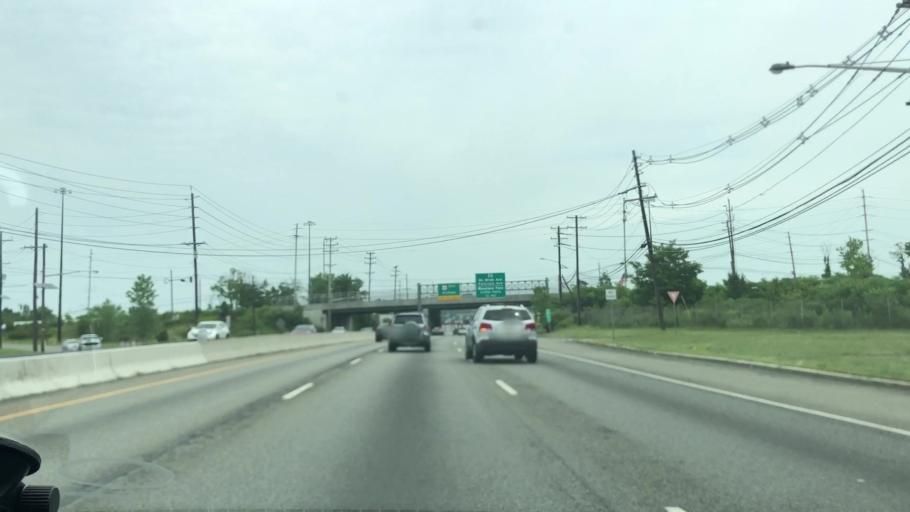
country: US
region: New Jersey
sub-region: Passaic County
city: Singac
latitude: 40.8936
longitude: -74.2277
